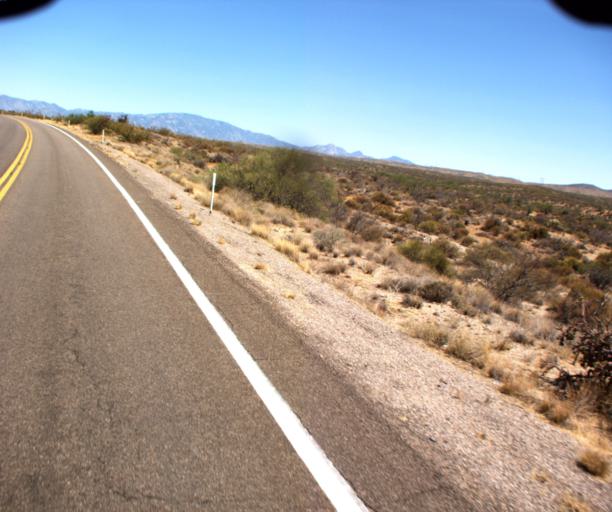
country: US
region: Arizona
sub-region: Pima County
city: Catalina
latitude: 32.6493
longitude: -111.0293
